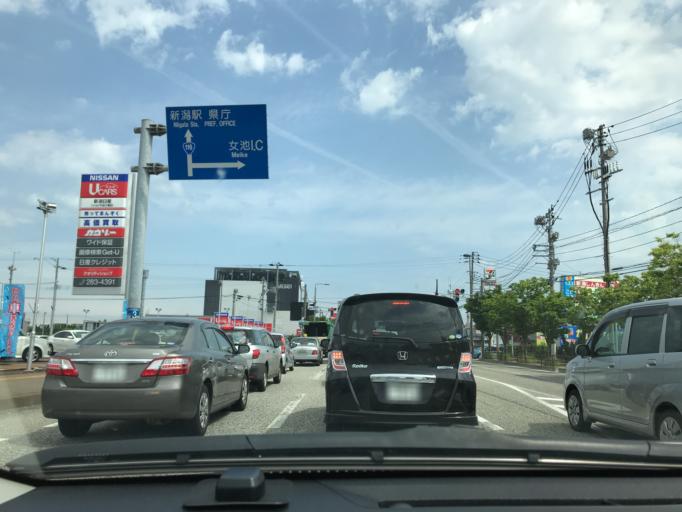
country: JP
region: Niigata
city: Niigata-shi
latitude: 37.8856
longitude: 139.0189
